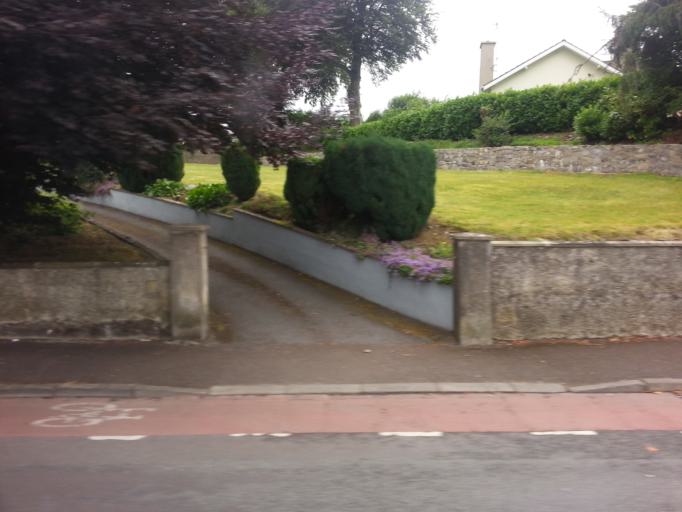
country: IE
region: Leinster
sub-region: Kilkenny
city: Kilkenny
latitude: 52.6457
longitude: -7.2402
